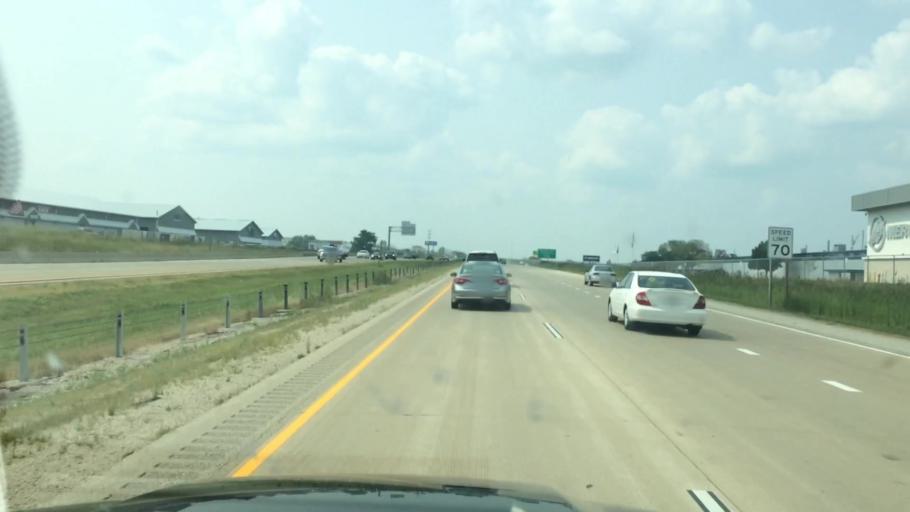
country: US
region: Wisconsin
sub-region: Fond du Lac County
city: Fond du Lac
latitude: 43.7535
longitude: -88.4676
